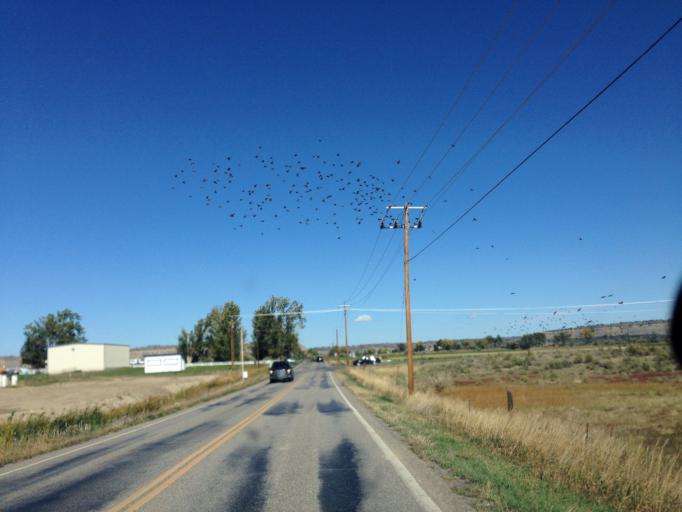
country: US
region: Montana
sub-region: Yellowstone County
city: Laurel
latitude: 45.7684
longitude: -108.6796
